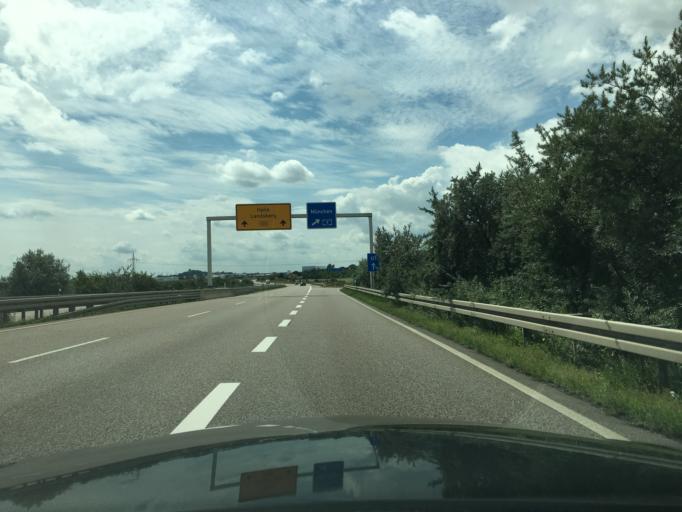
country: DE
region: Saxony-Anhalt
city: Brehna
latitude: 51.5552
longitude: 12.1876
